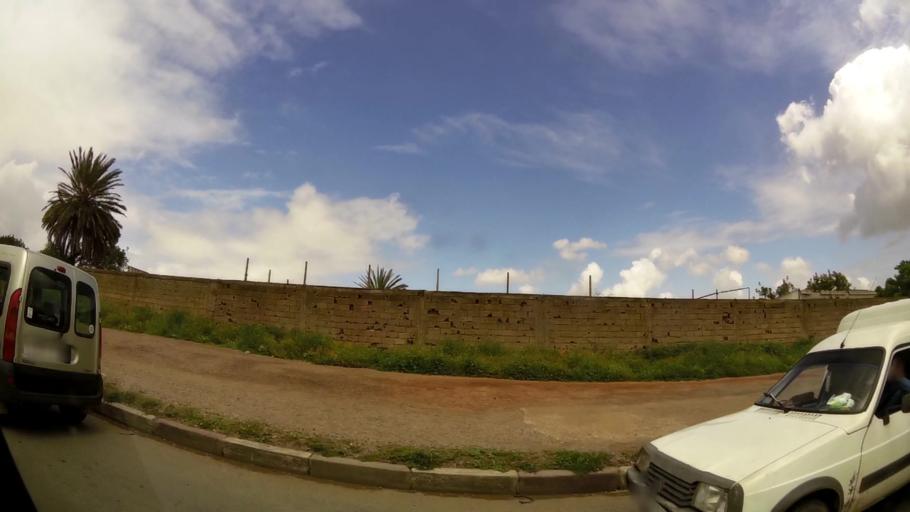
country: MA
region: Grand Casablanca
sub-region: Mediouna
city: Tit Mellil
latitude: 33.6061
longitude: -7.4942
